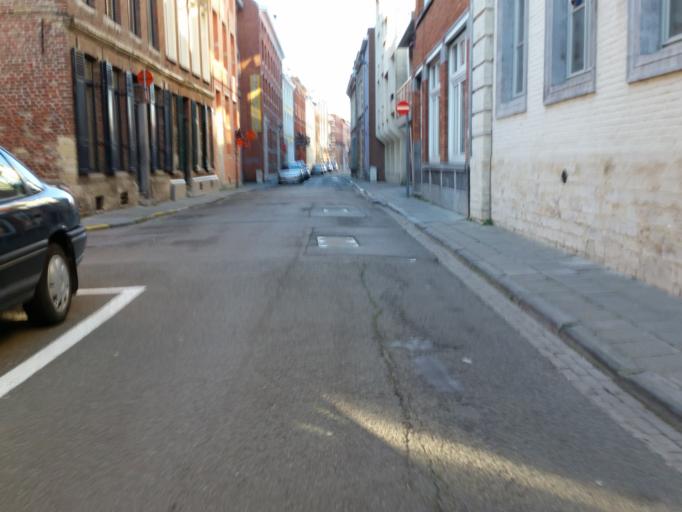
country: BE
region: Flanders
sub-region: Provincie Vlaams-Brabant
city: Leuven
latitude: 50.8817
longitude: 4.7015
